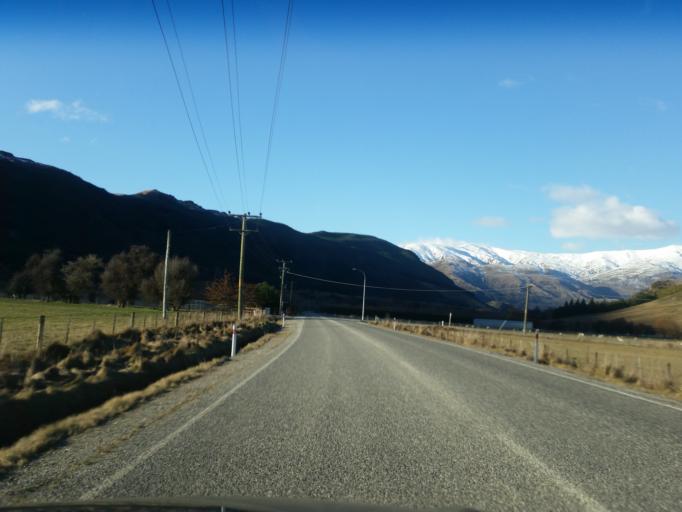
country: NZ
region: Otago
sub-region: Queenstown-Lakes District
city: Arrowtown
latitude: -44.9508
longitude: 168.7560
